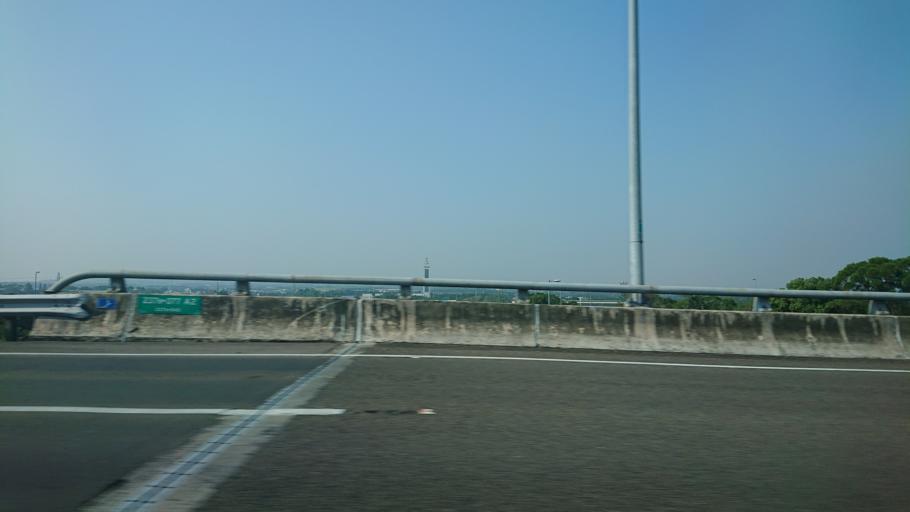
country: TW
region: Taiwan
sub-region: Nantou
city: Nantou
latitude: 23.8520
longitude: 120.7026
